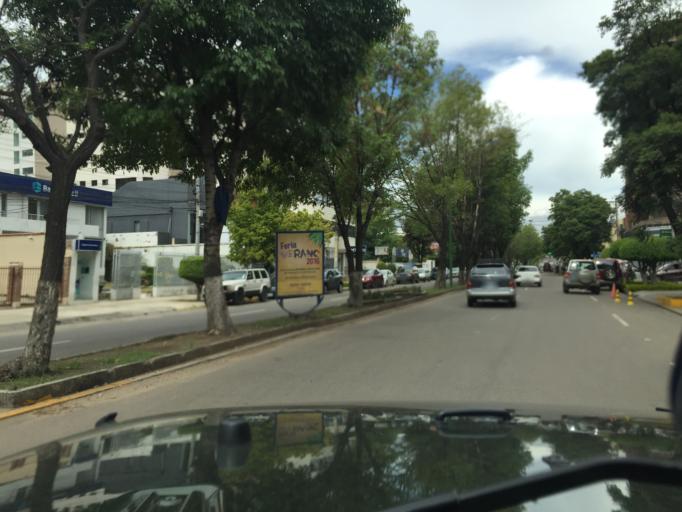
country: BO
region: Cochabamba
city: Cochabamba
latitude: -17.3729
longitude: -66.1565
